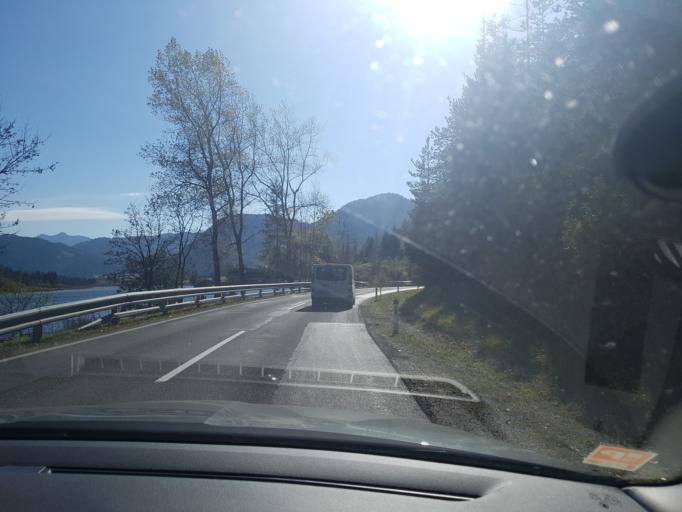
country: AT
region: Tyrol
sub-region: Politischer Bezirk Kitzbuhel
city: Waidring
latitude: 47.5425
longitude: 12.5674
